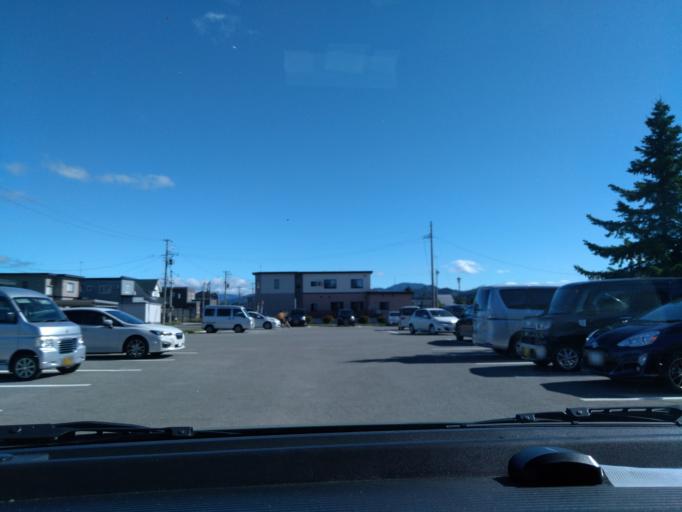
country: JP
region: Akita
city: Yuzawa
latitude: 39.2045
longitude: 140.5512
